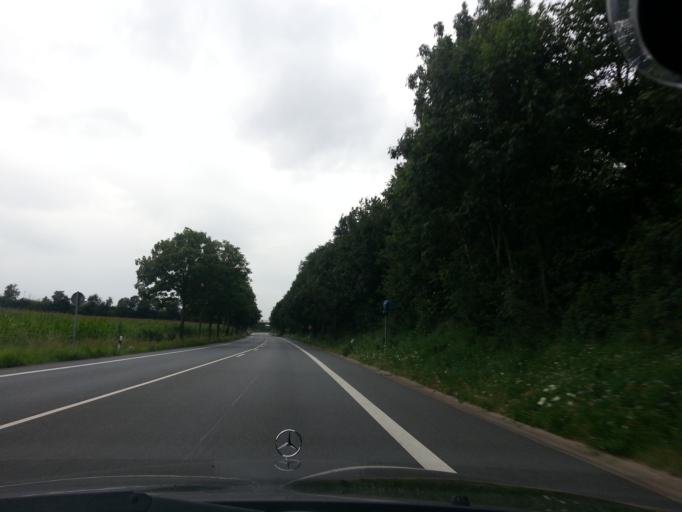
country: DE
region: North Rhine-Westphalia
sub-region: Regierungsbezirk Munster
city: Borken
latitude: 51.8317
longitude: 6.8470
